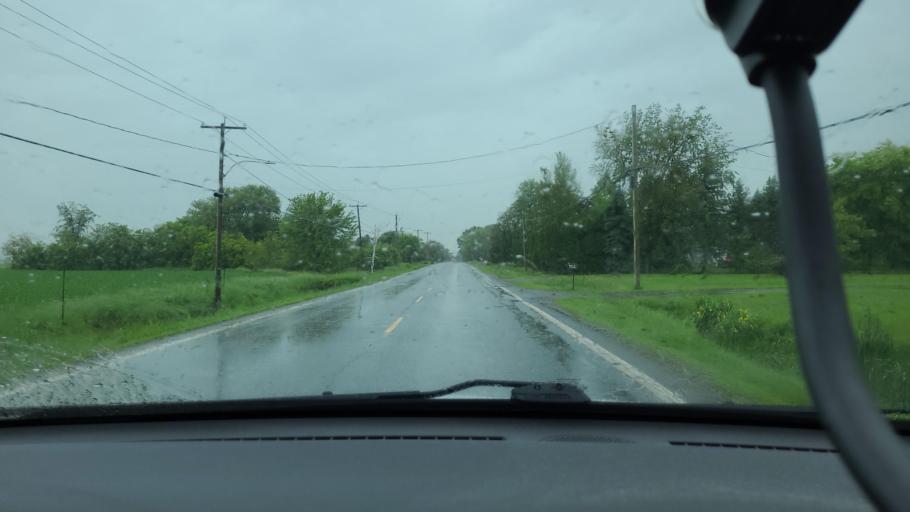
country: CA
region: Quebec
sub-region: Monteregie
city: Saint-Hyacinthe
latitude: 45.6164
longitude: -73.0317
